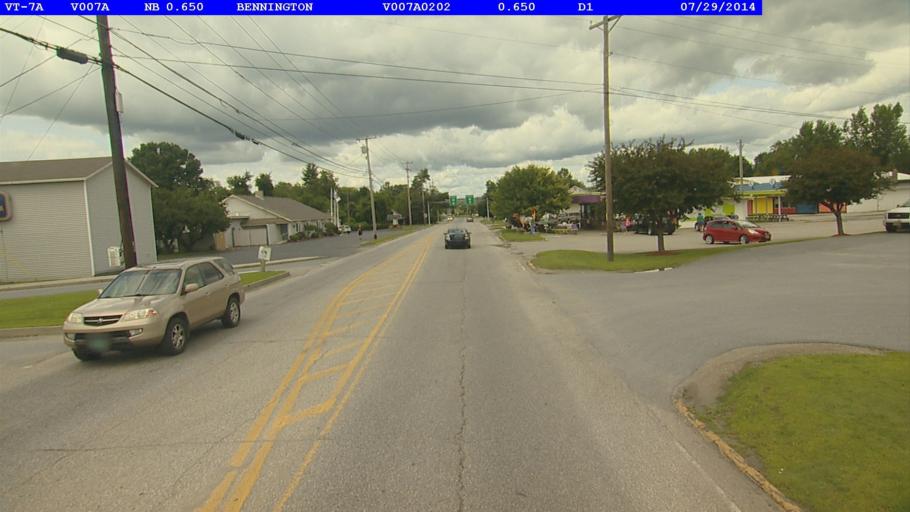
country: US
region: Vermont
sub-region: Bennington County
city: Bennington
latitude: 42.8997
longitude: -73.2102
